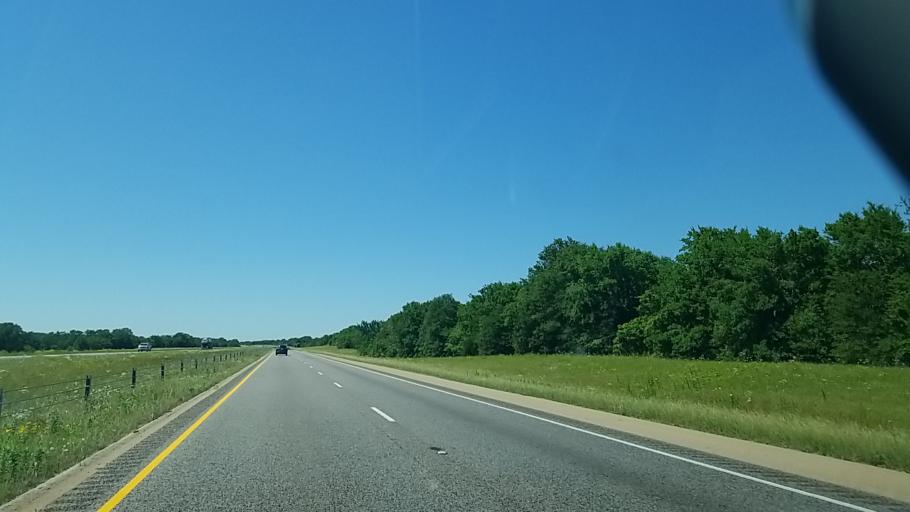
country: US
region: Texas
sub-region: Freestone County
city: Fairfield
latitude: 31.6750
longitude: -96.1639
